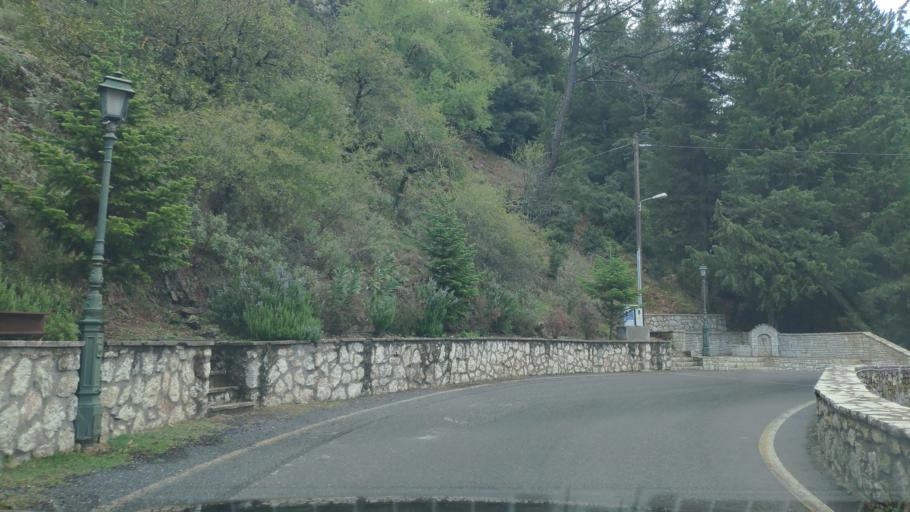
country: GR
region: Peloponnese
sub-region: Nomos Arkadias
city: Dimitsana
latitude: 37.5968
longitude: 22.0426
